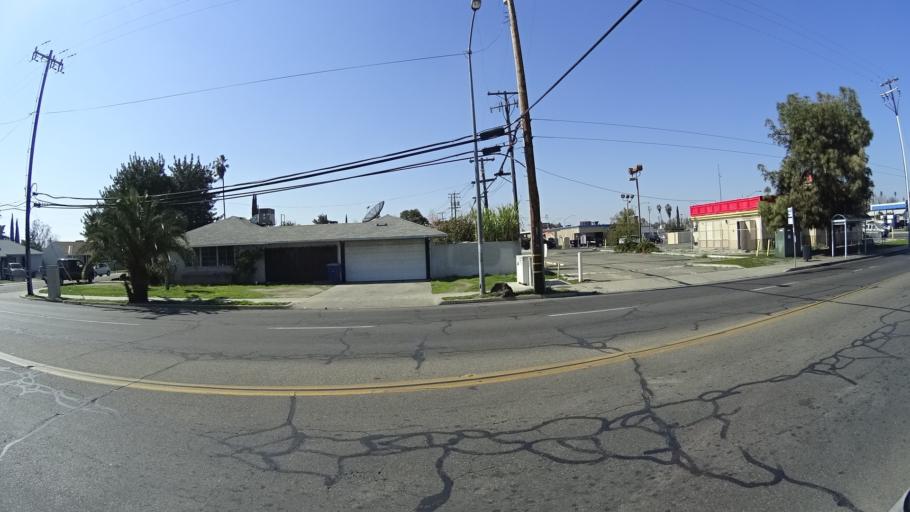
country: US
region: California
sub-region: Fresno County
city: Fresno
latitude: 36.7353
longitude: -119.7546
